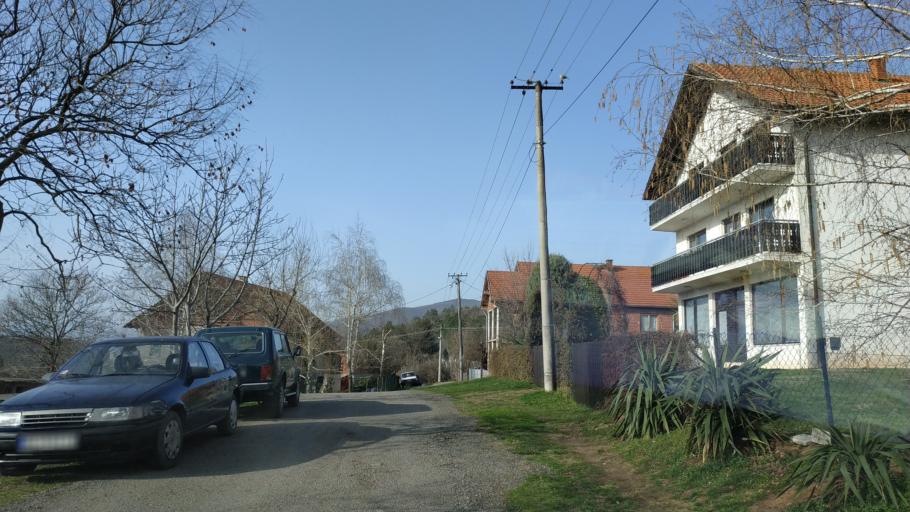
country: RS
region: Central Serbia
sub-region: Nisavski Okrug
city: Aleksinac
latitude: 43.5456
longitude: 21.7164
